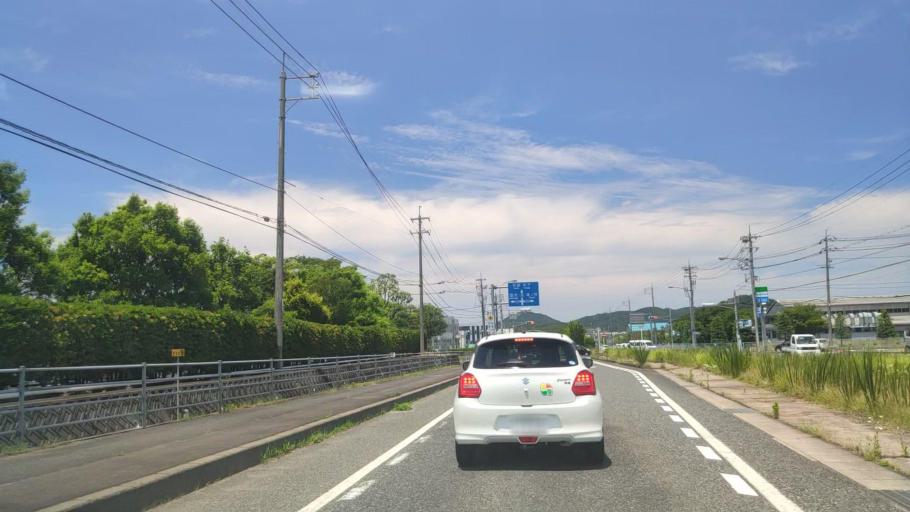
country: JP
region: Tottori
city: Tottori
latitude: 35.4571
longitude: 134.2430
